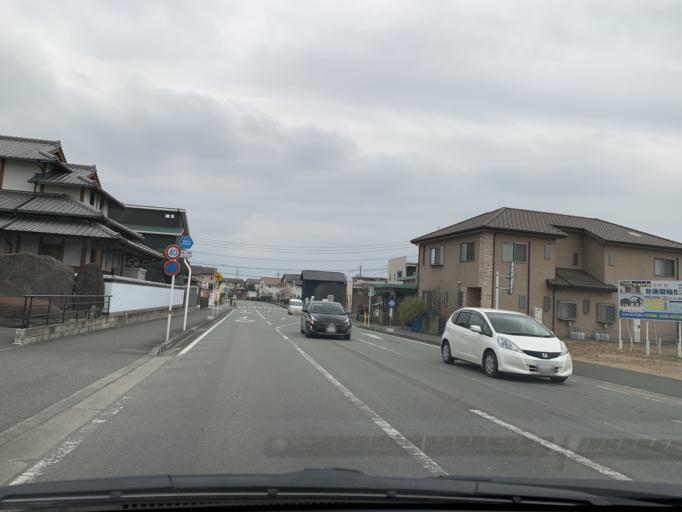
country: JP
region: Kumamoto
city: Ozu
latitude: 32.8889
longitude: 130.8814
